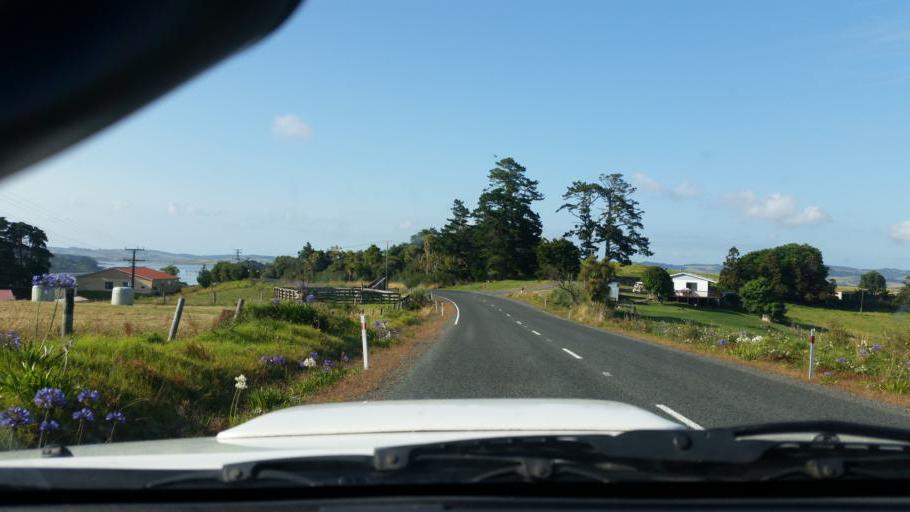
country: NZ
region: Northland
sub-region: Whangarei
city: Ruakaka
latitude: -36.1274
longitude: 174.2302
